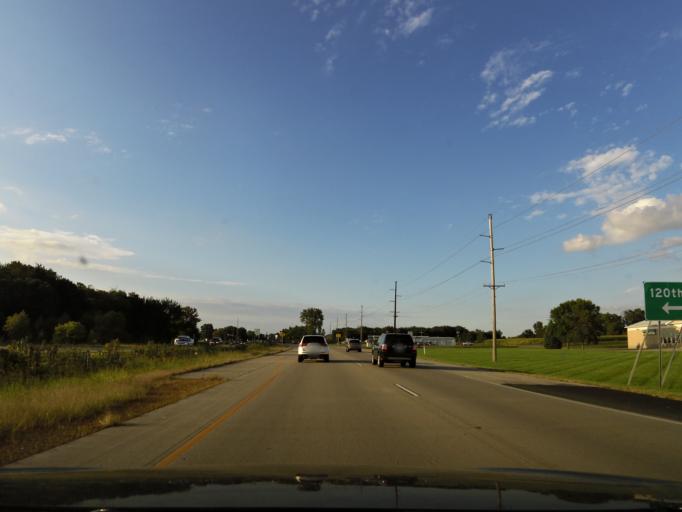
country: US
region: Minnesota
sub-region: Dakota County
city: Hastings
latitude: 44.7739
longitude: -92.8629
